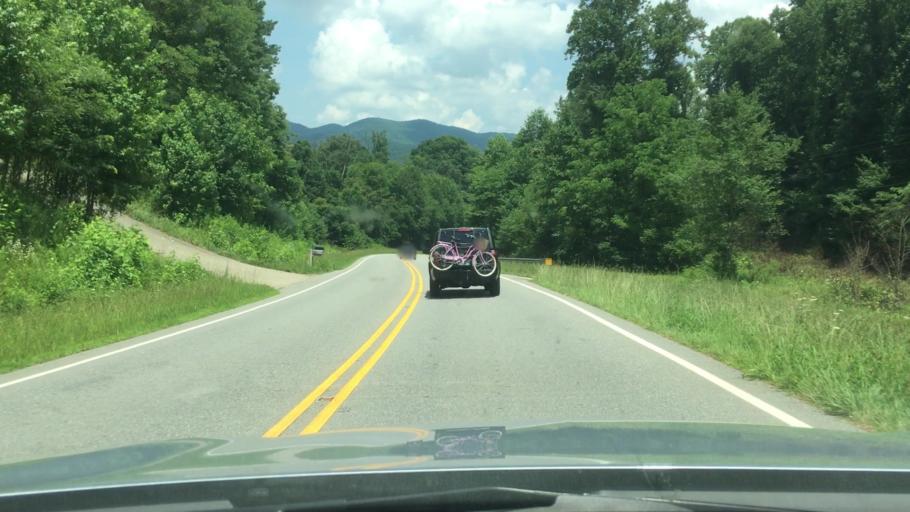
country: US
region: North Carolina
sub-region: Madison County
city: Marshall
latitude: 35.9045
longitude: -82.8771
